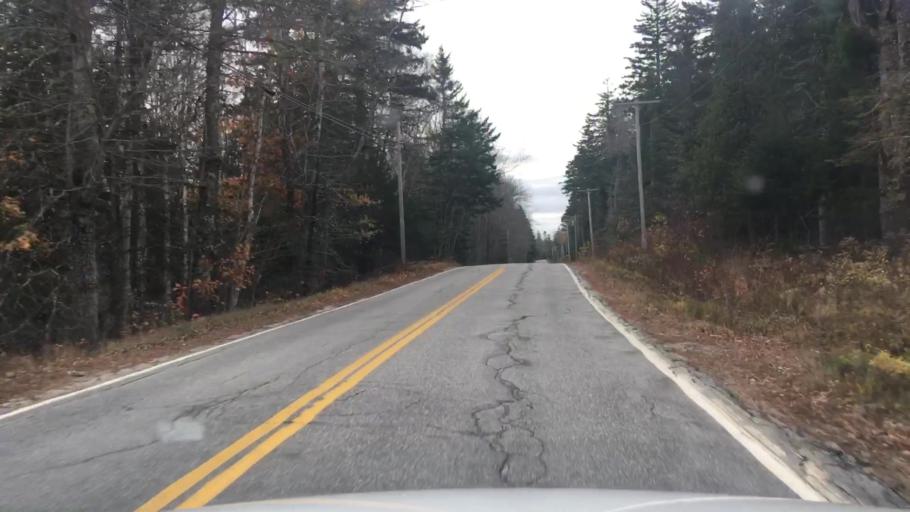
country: US
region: Maine
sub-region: Hancock County
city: Sedgwick
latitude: 44.3005
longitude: -68.5600
